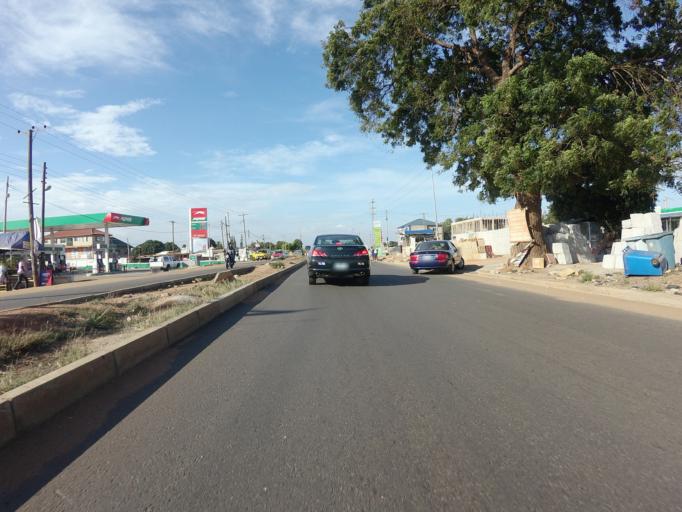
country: GH
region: Greater Accra
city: Nungua
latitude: 5.6390
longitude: -0.0621
